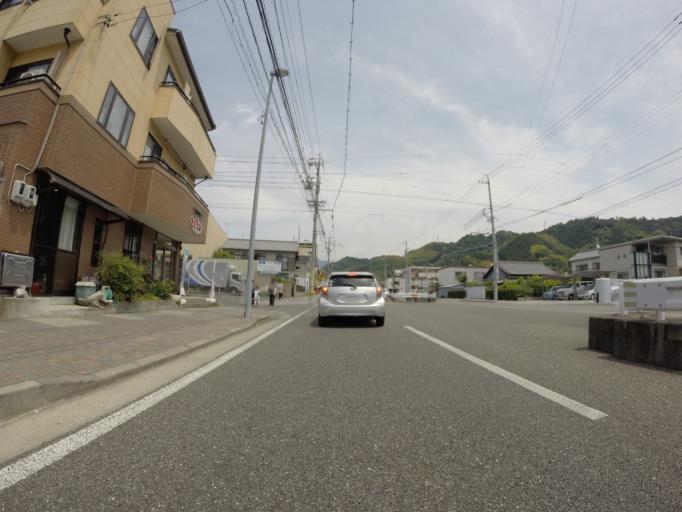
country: JP
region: Shizuoka
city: Shizuoka-shi
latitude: 35.0098
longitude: 138.3733
